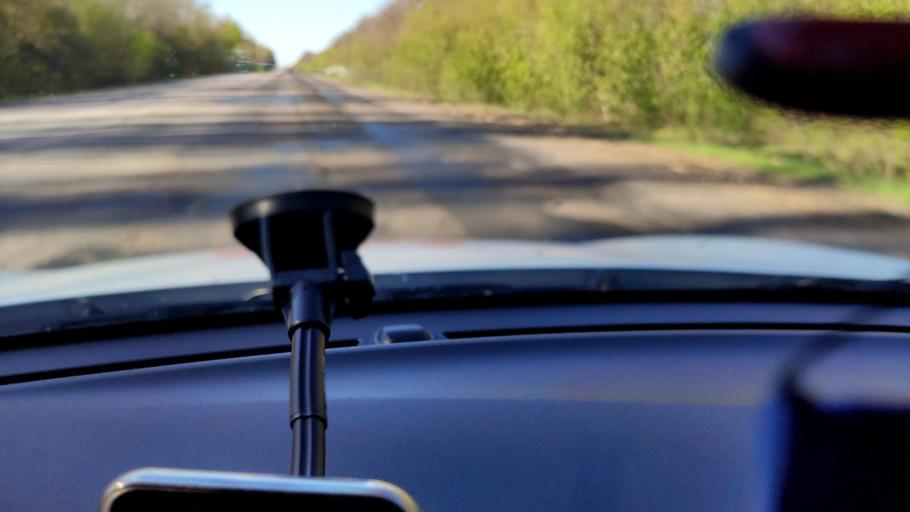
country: RU
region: Voronezj
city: Kolodeznyy
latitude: 51.2476
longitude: 39.0554
